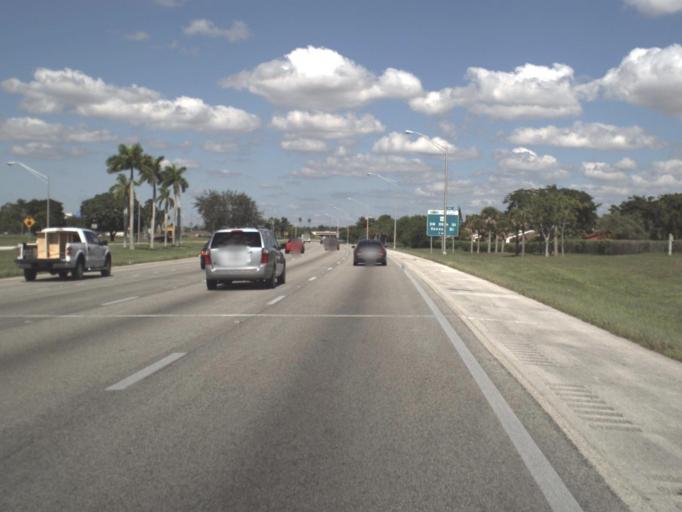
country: US
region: Florida
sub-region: Miami-Dade County
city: The Crossings
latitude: 25.6639
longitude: -80.3861
